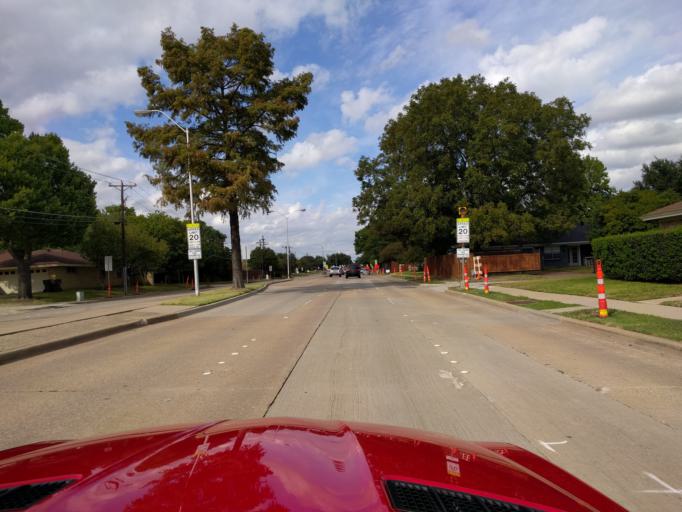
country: US
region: Texas
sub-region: Collin County
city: Plano
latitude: 33.0105
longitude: -96.7338
